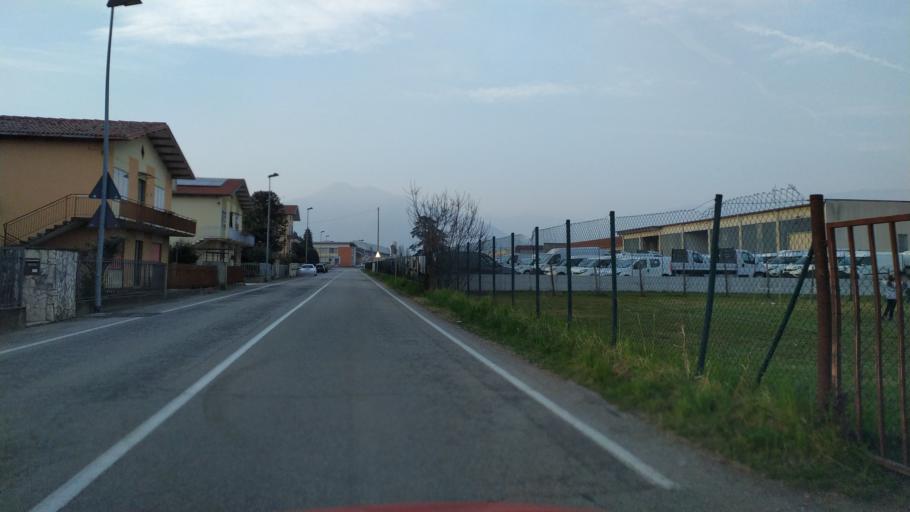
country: IT
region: Veneto
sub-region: Provincia di Vicenza
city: Marano Vicentino
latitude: 45.6909
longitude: 11.4434
